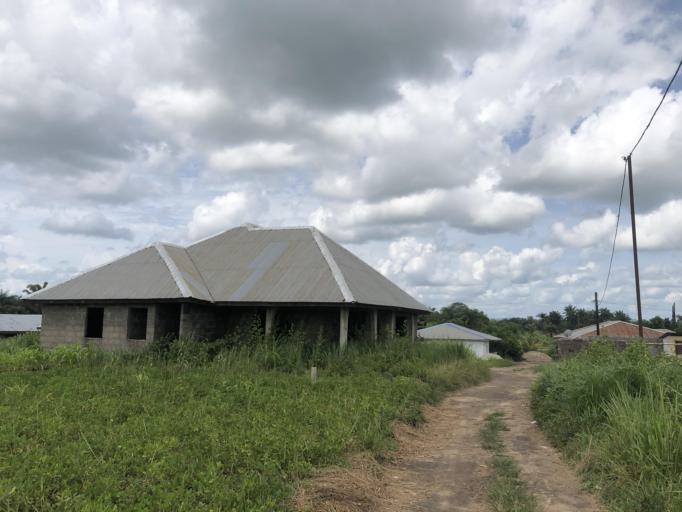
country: SL
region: Northern Province
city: Magburaka
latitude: 8.7135
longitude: -11.9256
